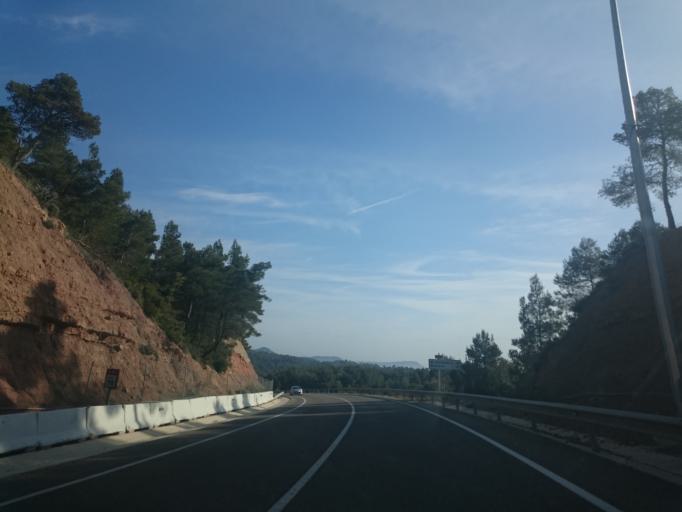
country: ES
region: Catalonia
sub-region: Provincia de Barcelona
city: Castellfollit del Boix
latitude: 41.6350
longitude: 1.6953
